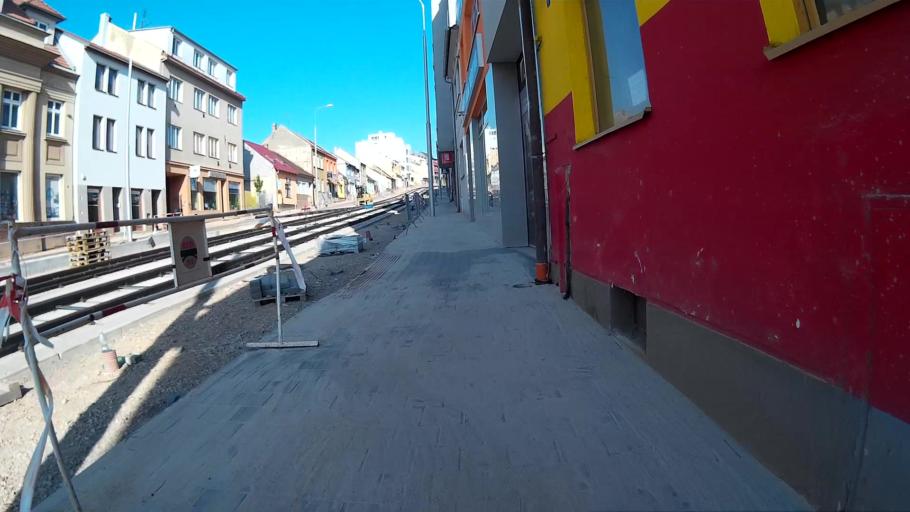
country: CZ
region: South Moravian
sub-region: Mesto Brno
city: Brno
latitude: 49.2121
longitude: 16.5796
